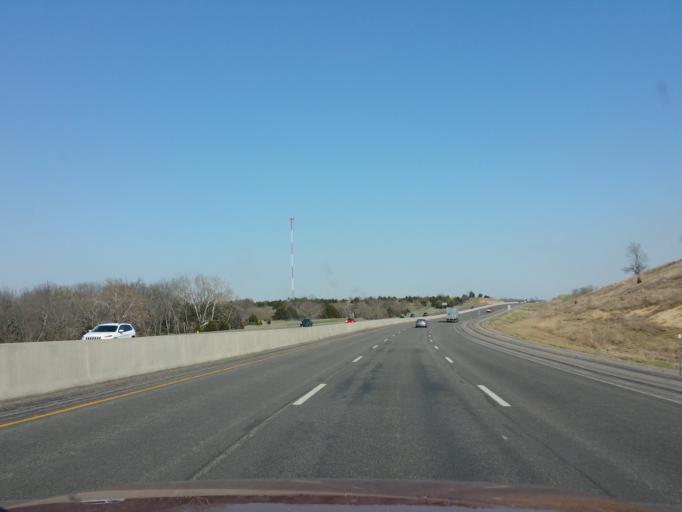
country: US
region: Kansas
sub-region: Shawnee County
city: Topeka
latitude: 39.0179
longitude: -95.4945
